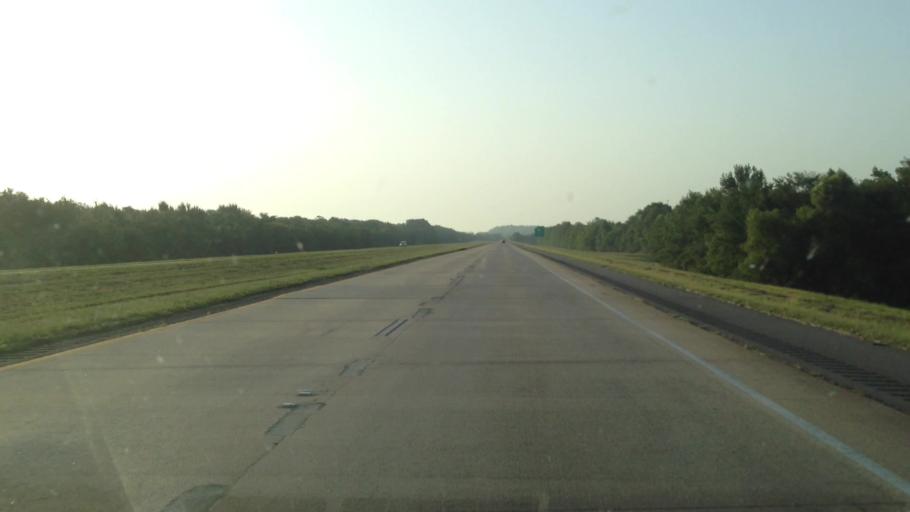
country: US
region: Louisiana
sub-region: Grant Parish
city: Colfax
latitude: 31.5066
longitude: -92.8857
